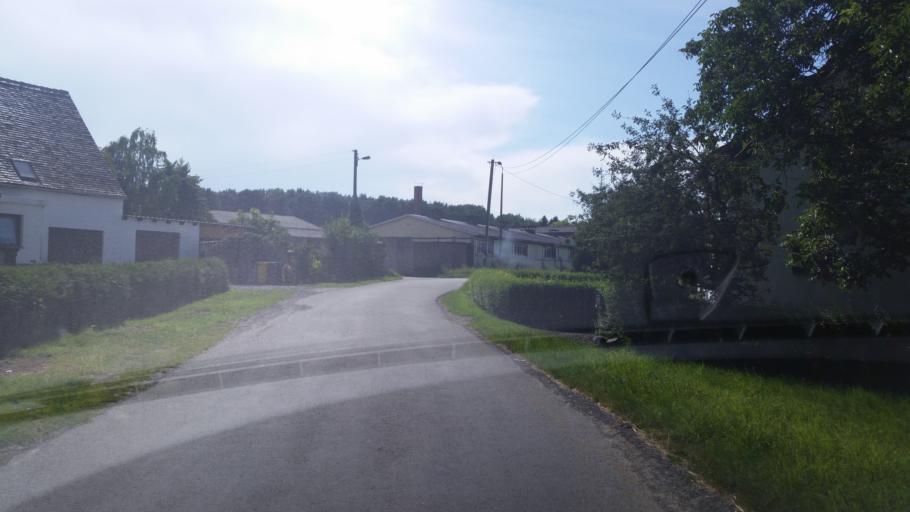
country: DE
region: Saxony
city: Kamenz
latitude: 51.3099
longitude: 14.0465
